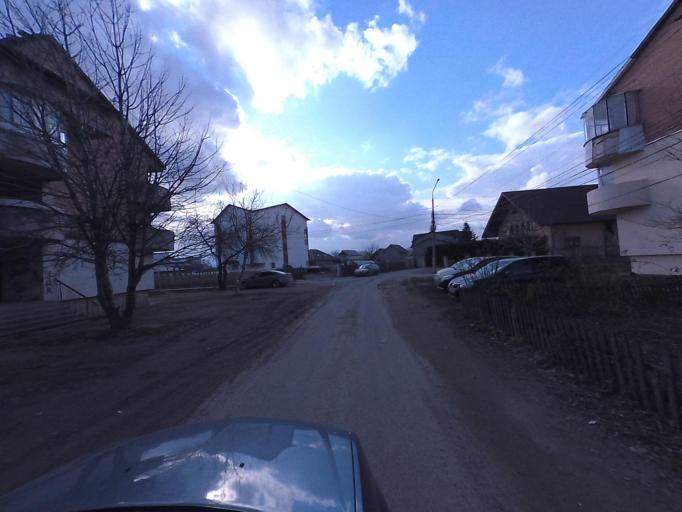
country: RO
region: Neamt
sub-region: Oras Targu Neamt
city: Targu Neamt
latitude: 47.2039
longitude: 26.3751
